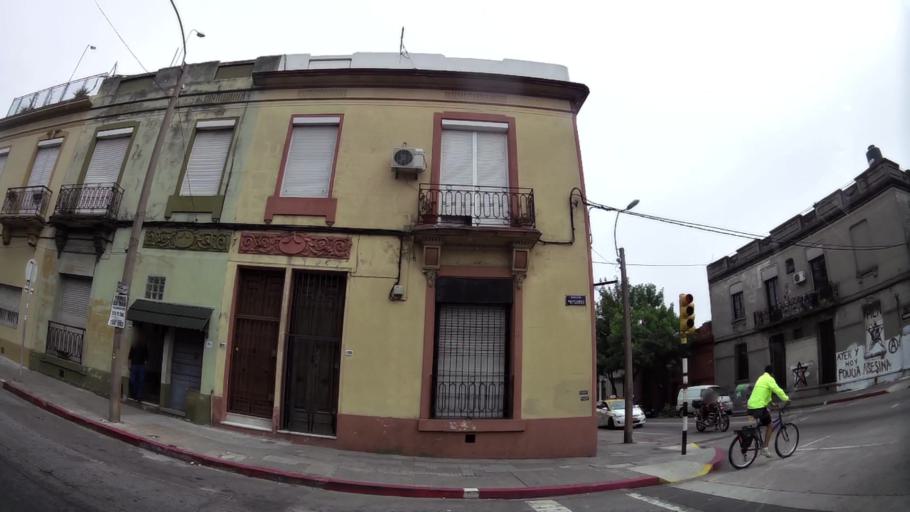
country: UY
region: Montevideo
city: Montevideo
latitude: -34.8979
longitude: -56.1773
